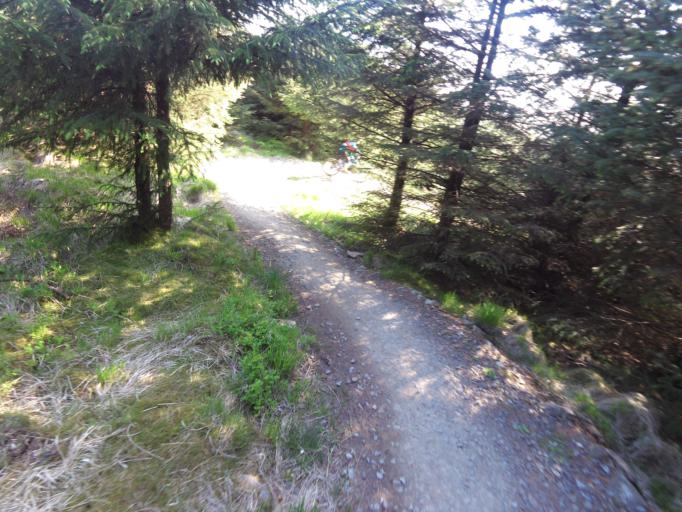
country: GB
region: England
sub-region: North Yorkshire
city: Settle
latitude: 54.0292
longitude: -2.3711
